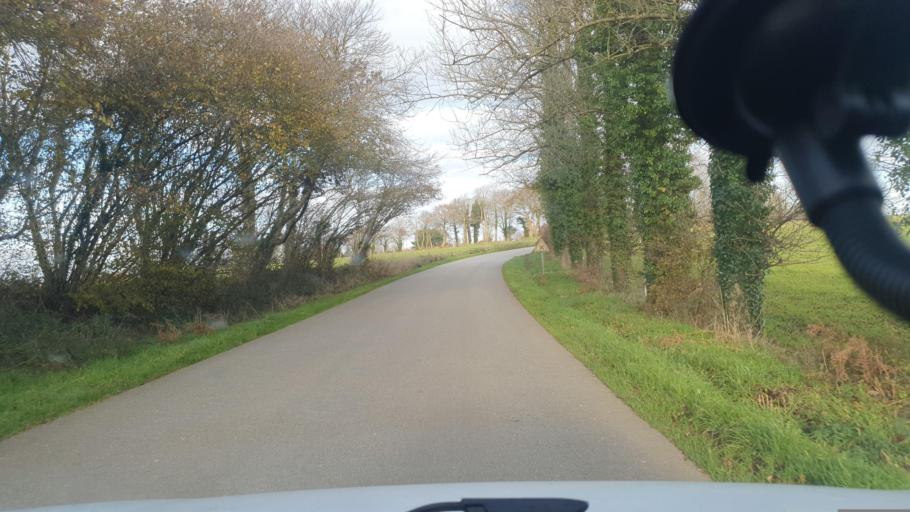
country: FR
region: Brittany
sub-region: Departement du Finistere
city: Briec
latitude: 48.0690
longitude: -4.0165
